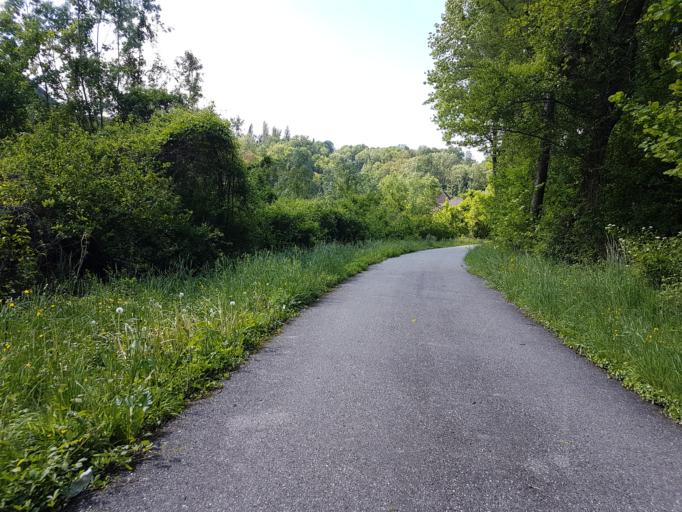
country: FR
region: Rhone-Alpes
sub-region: Departement de l'Ain
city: Culoz
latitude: 45.8107
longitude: 5.7915
